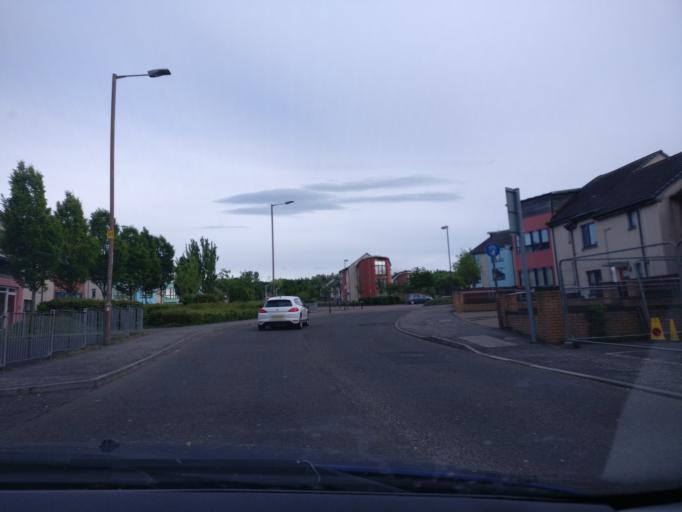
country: GB
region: Scotland
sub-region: West Lothian
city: Seafield
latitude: 55.9321
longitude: -3.1409
